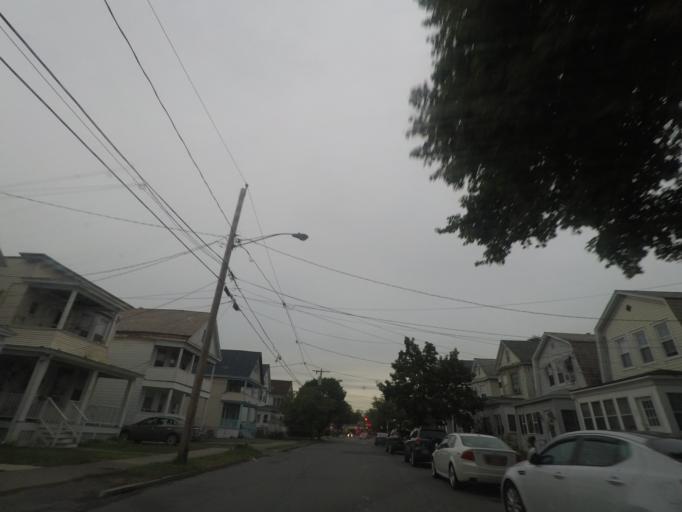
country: US
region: New York
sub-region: Albany County
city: Albany
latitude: 42.6385
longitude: -73.7850
